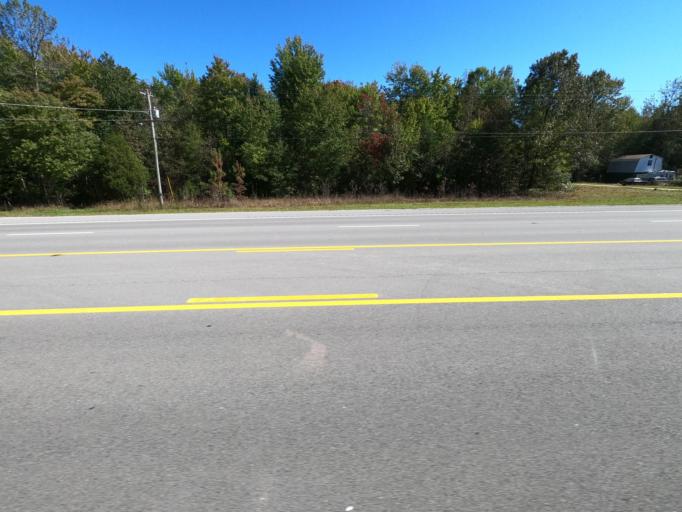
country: US
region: Tennessee
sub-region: Maury County
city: Mount Pleasant
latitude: 35.4367
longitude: -87.2801
